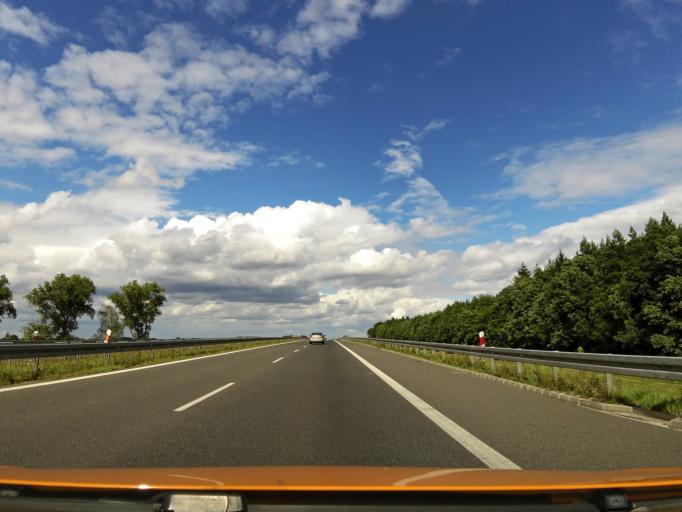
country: PL
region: West Pomeranian Voivodeship
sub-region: Powiat goleniowski
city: Nowogard
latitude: 53.6710
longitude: 15.0783
